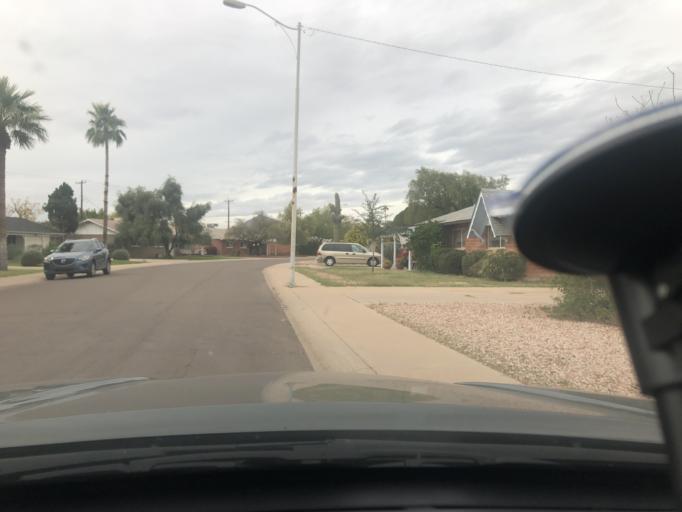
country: US
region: Arizona
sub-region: Maricopa County
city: Scottsdale
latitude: 33.4820
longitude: -111.8983
